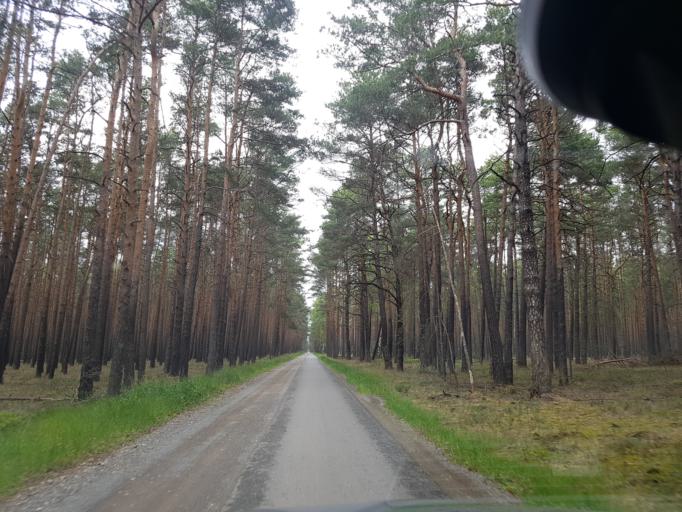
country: DE
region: Brandenburg
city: Crinitz
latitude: 51.6665
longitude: 13.7839
